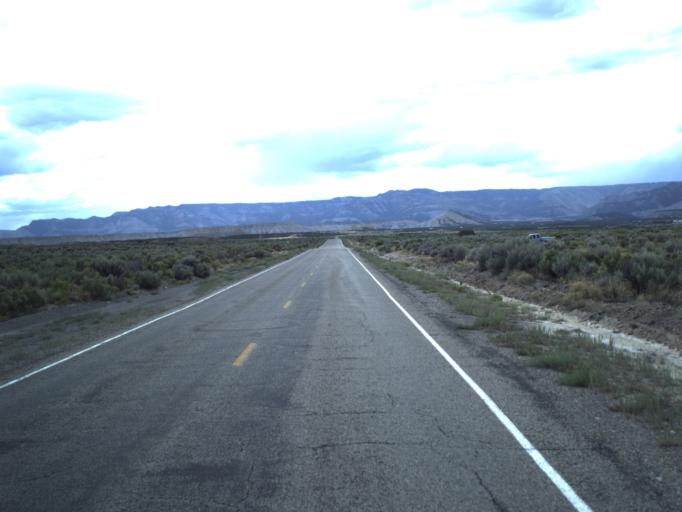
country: US
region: Utah
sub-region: Carbon County
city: Price
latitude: 39.4909
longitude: -110.8572
